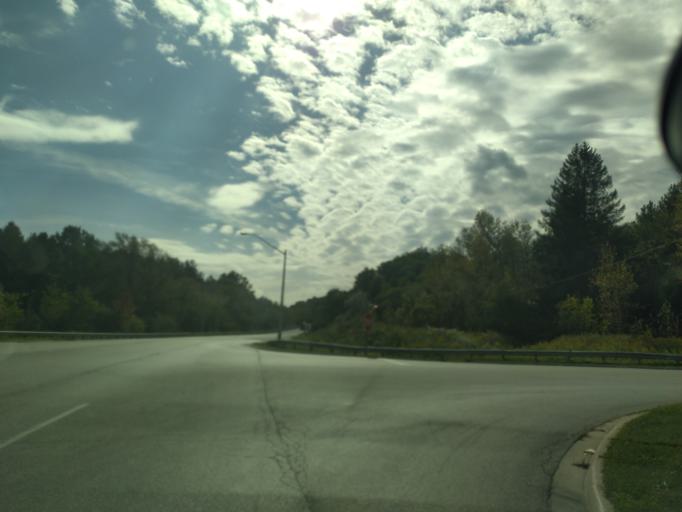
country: CA
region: Ontario
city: Newmarket
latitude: 44.0918
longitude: -79.4897
